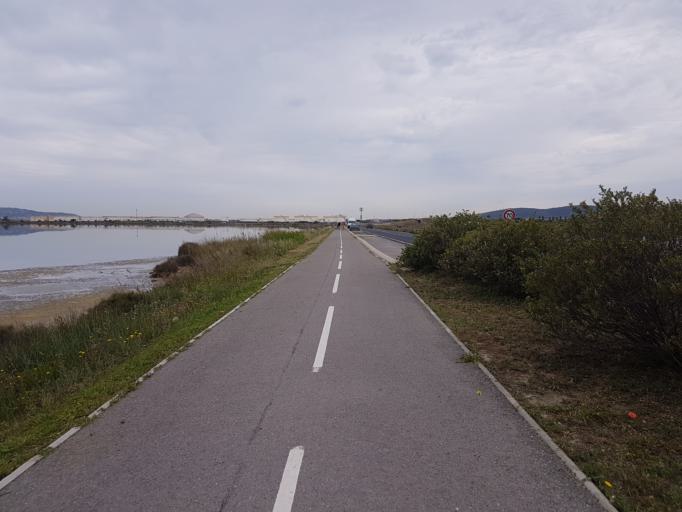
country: FR
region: Languedoc-Roussillon
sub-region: Departement de l'Herault
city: Frontignan
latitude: 43.4355
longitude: 3.7707
